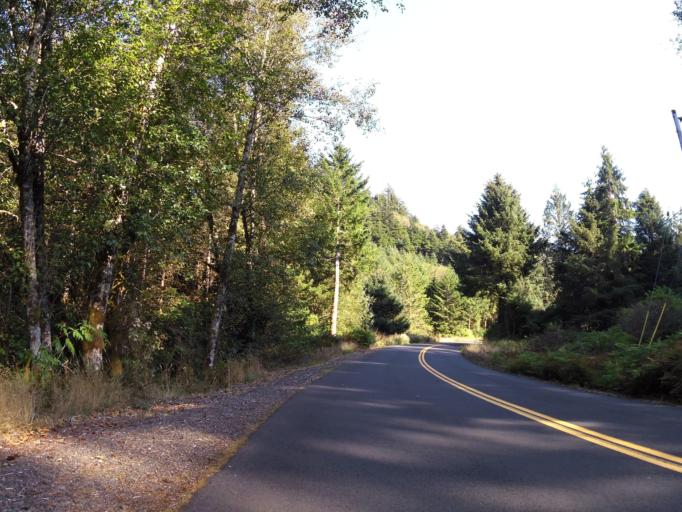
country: US
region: Oregon
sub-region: Lincoln County
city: Rose Lodge
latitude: 45.0829
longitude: -123.9464
